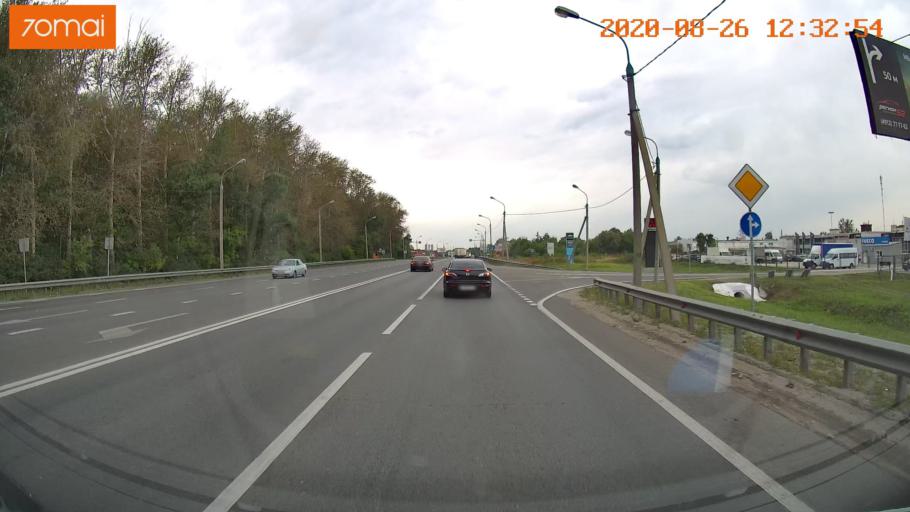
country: RU
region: Rjazan
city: Ryazan'
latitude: 54.5797
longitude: 39.7828
